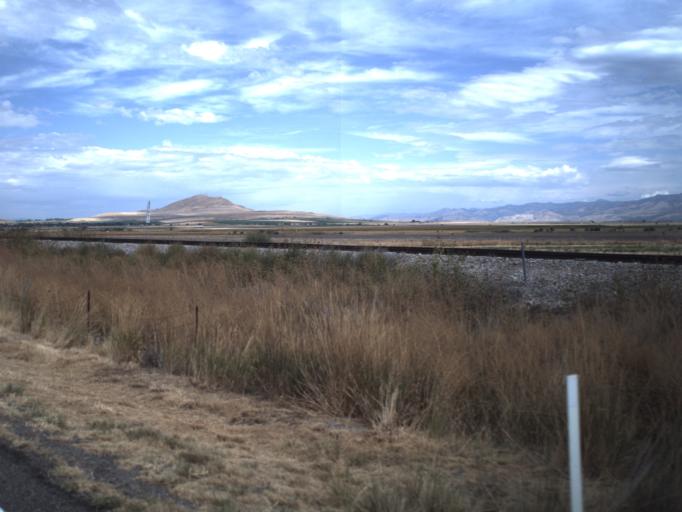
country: US
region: Utah
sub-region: Cache County
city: Benson
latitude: 41.8072
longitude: -111.9940
